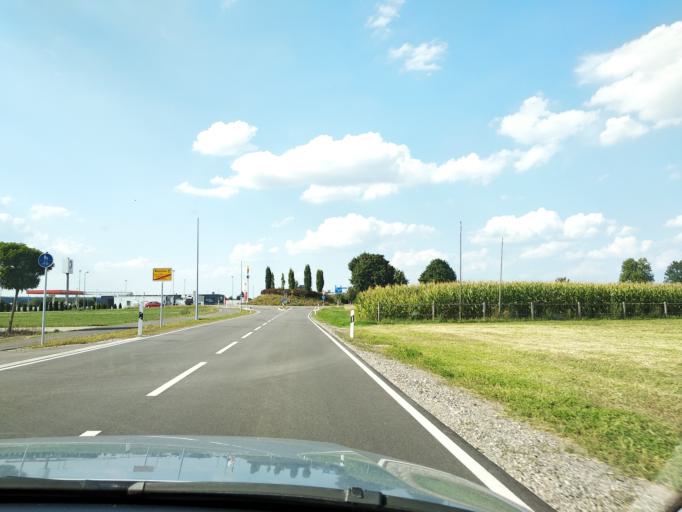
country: DE
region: Bavaria
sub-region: Swabia
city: Holzgunz
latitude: 48.0171
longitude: 10.2747
